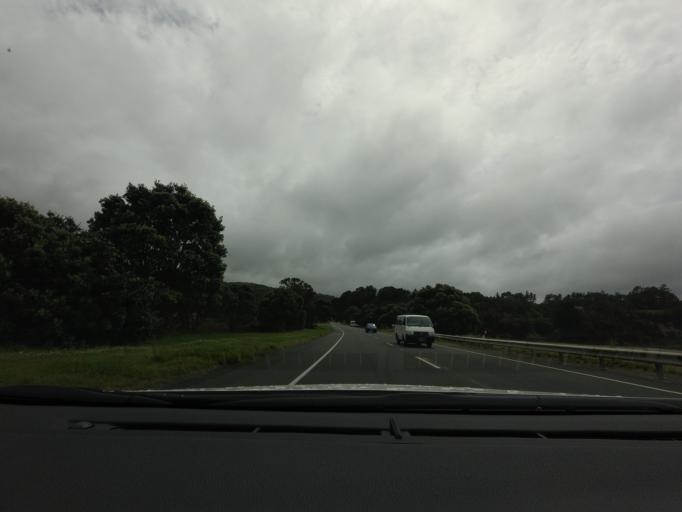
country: NZ
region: Auckland
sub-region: Auckland
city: Warkworth
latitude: -36.5636
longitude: 174.6957
